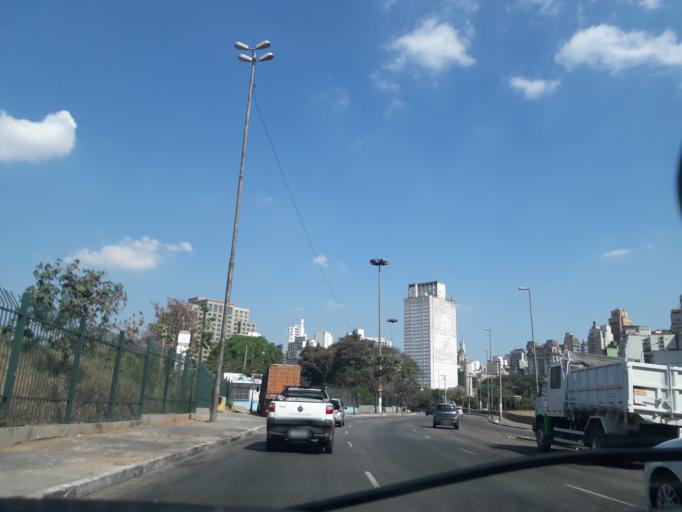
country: BR
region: Sao Paulo
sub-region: Sao Paulo
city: Sao Paulo
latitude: -23.5441
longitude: -46.6295
